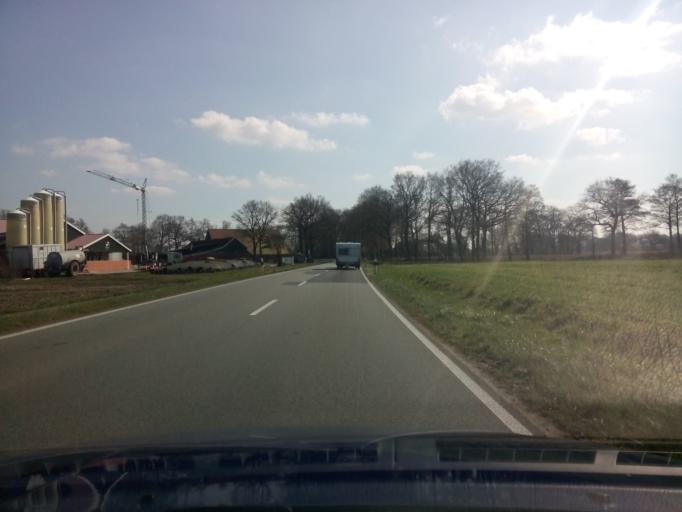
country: DE
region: Lower Saxony
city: Golenkamp
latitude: 52.5436
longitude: 6.9328
